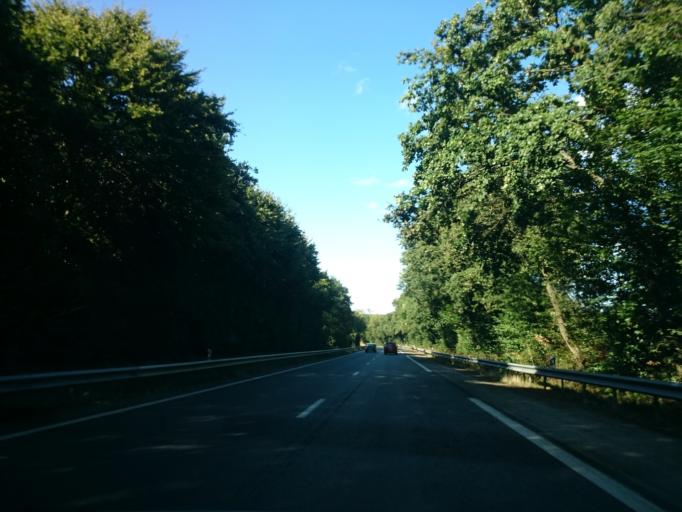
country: FR
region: Brittany
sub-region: Departement d'Ille-et-Vilaine
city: La Dominelais
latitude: 47.7958
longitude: -1.6902
